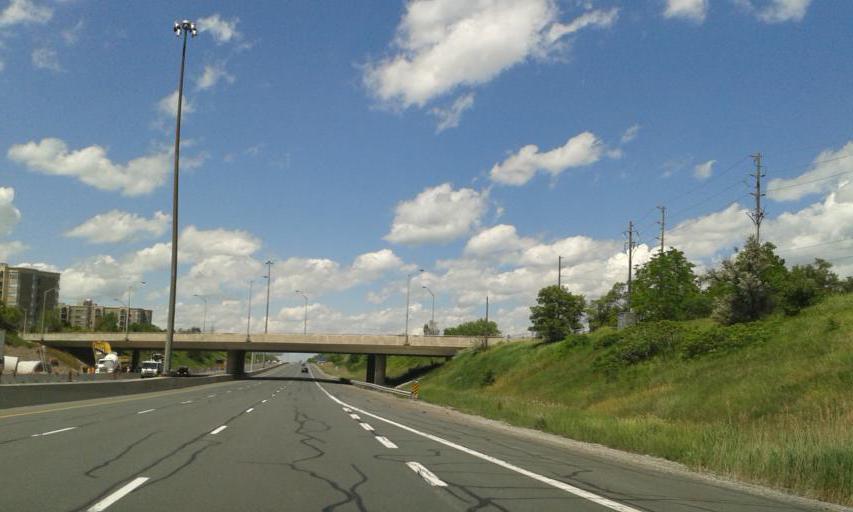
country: CA
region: Ontario
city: Burlington
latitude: 43.3464
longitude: -79.8310
